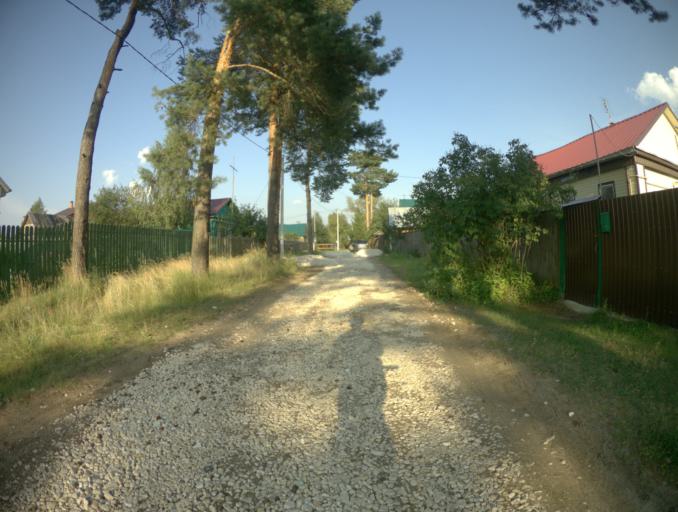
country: RU
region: Vladimir
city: Raduzhnyy
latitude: 56.0292
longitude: 40.3894
